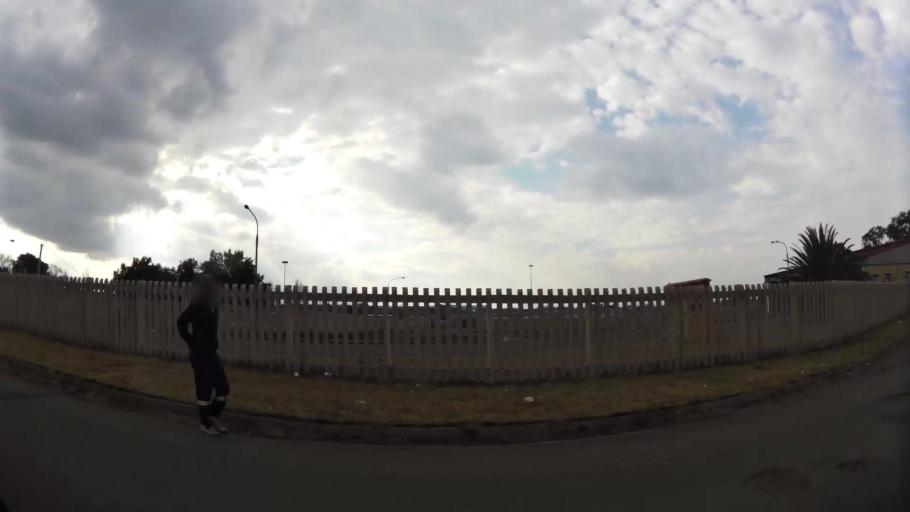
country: ZA
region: Gauteng
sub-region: Sedibeng District Municipality
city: Vanderbijlpark
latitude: -26.6712
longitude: 27.8395
